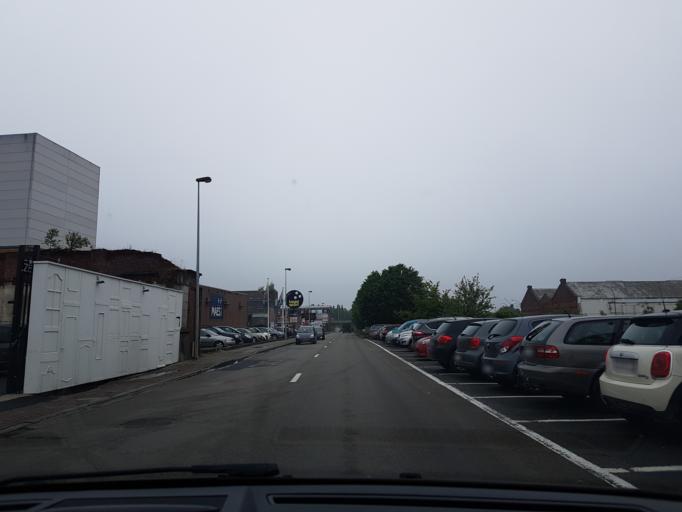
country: BE
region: Flanders
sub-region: Provincie Oost-Vlaanderen
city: Aalst
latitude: 50.9462
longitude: 4.0380
